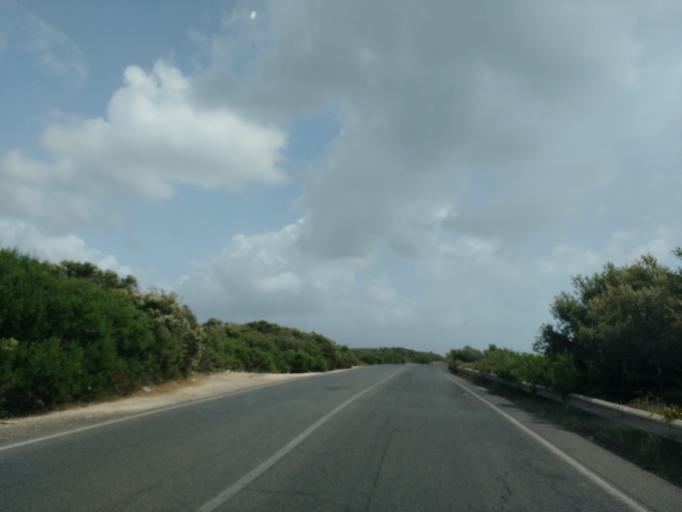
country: IT
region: Latium
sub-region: Citta metropolitana di Roma Capitale
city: Torvaianica
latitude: 41.6738
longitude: 12.3937
